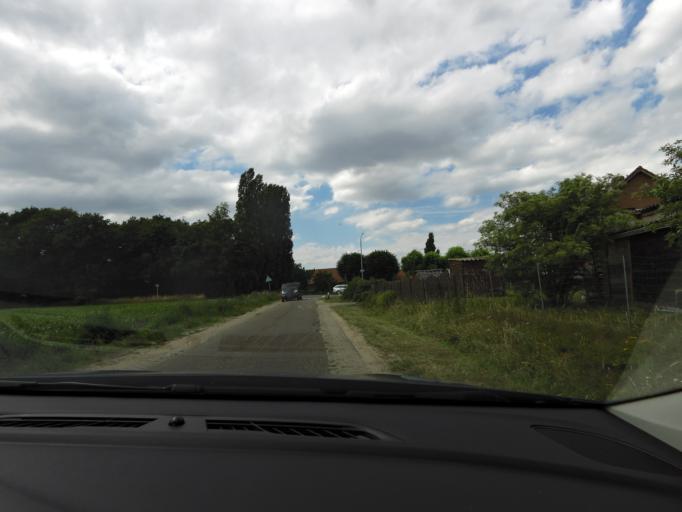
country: NL
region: North Brabant
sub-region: Gemeente Baarle-Nassau
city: Baarle-Nassau
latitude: 51.4350
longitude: 4.9155
